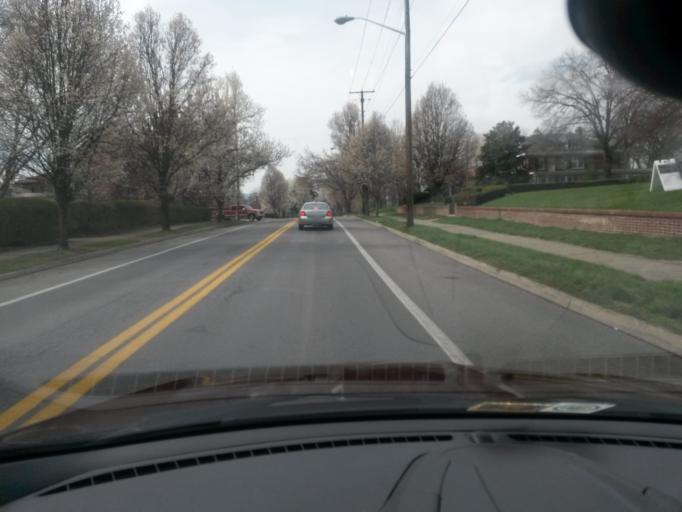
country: US
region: Virginia
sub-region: City of Roanoke
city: Roanoke
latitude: 37.2596
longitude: -79.9809
